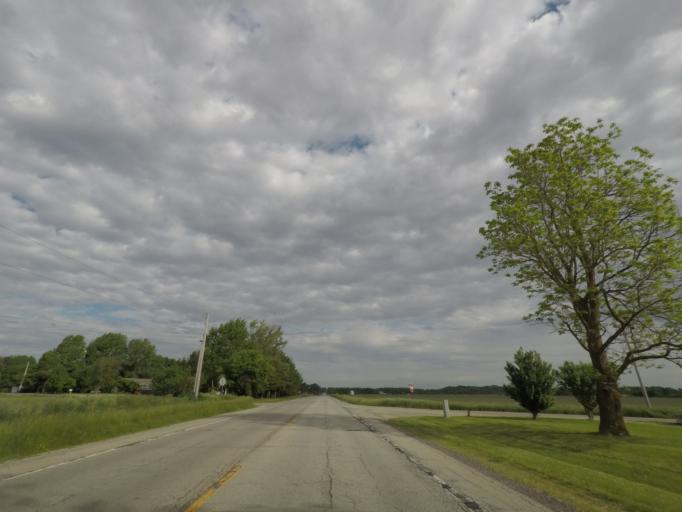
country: US
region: Illinois
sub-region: Logan County
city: Lincoln
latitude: 40.1063
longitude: -89.3238
